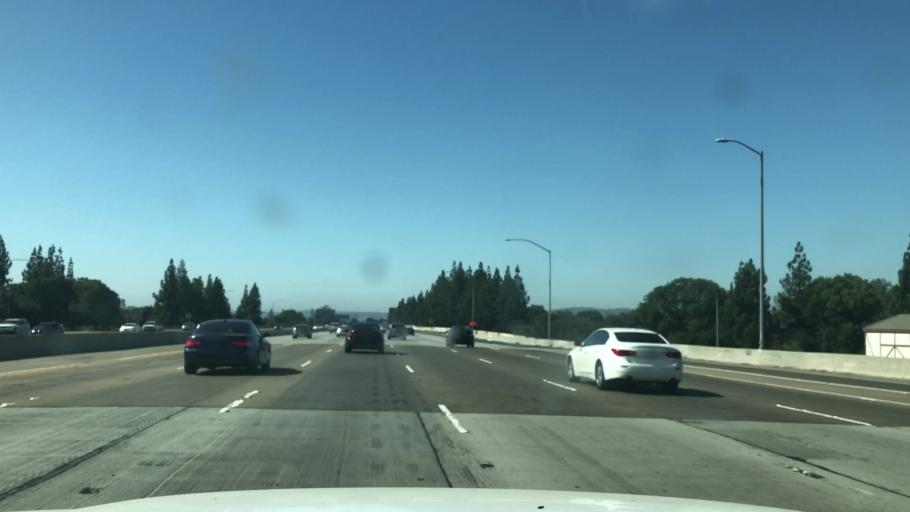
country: US
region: California
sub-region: Los Angeles County
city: San Fernando
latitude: 34.2576
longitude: -118.4724
